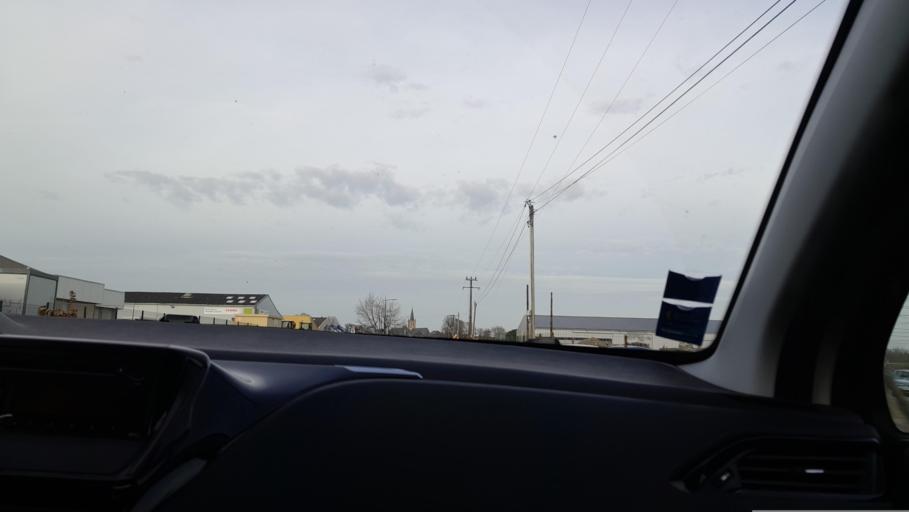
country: FR
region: Pays de la Loire
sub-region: Departement de la Mayenne
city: Ballots
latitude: 47.8918
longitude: -1.0409
